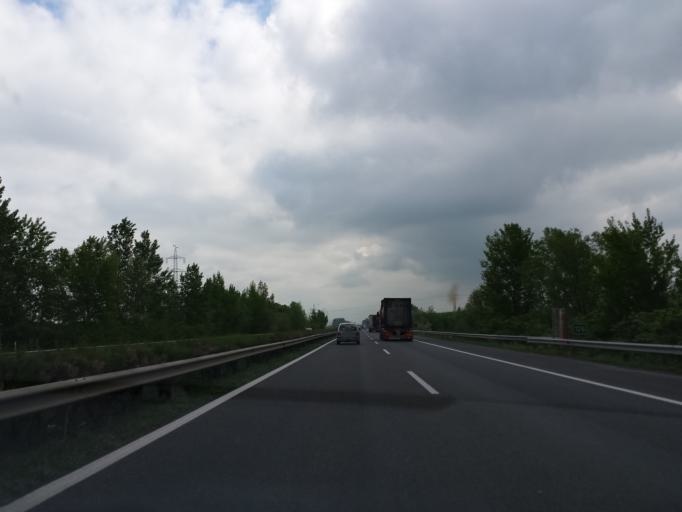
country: HU
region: Gyor-Moson-Sopron
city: Abda
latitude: 47.6617
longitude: 17.5826
